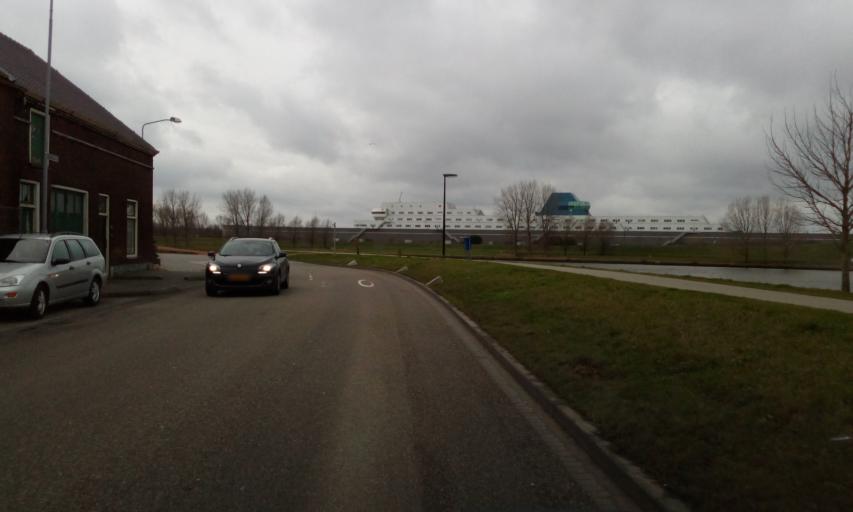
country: NL
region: South Holland
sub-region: Gemeente Ridderkerk
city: Ridderkerk
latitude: 51.8811
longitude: 4.6286
